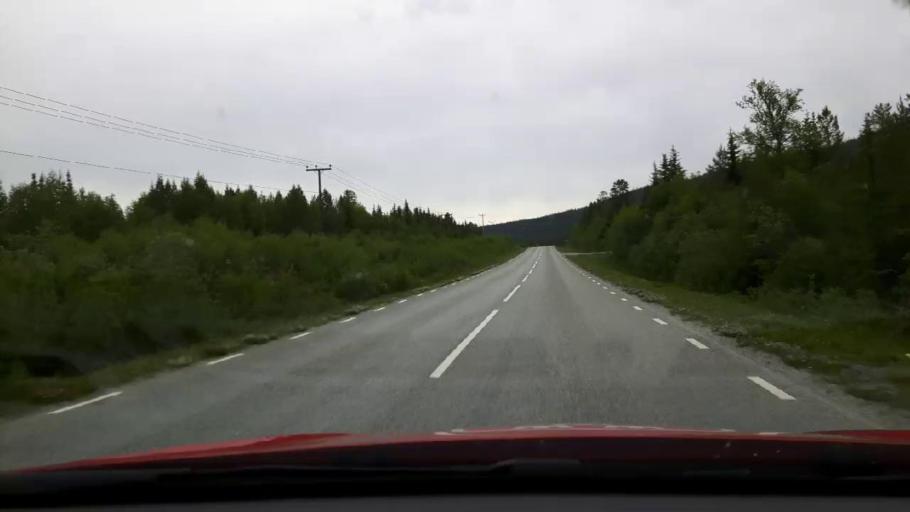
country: SE
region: Jaemtland
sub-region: Are Kommun
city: Are
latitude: 62.5721
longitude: 12.5603
